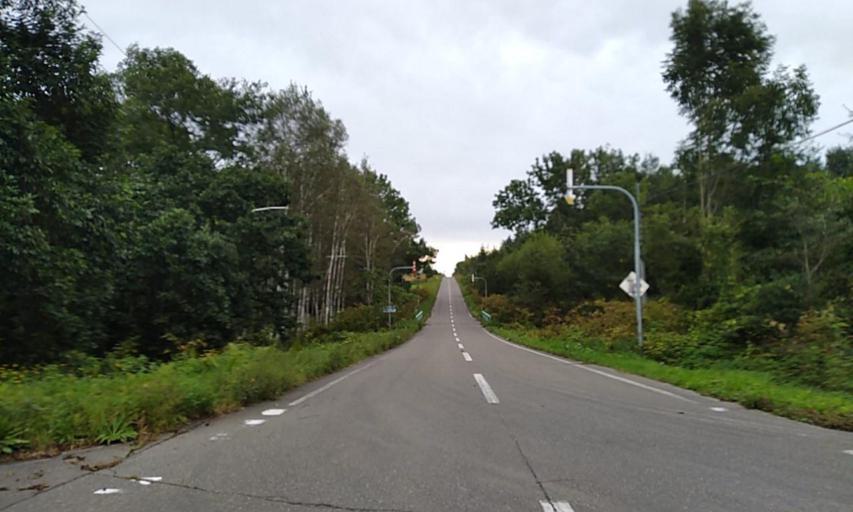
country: JP
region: Hokkaido
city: Obihiro
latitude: 42.6652
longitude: 143.0674
